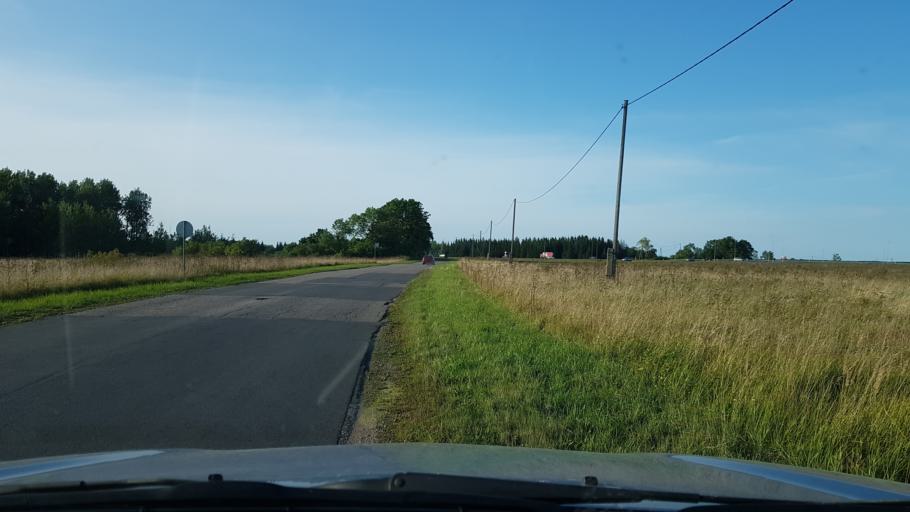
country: EE
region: Ida-Virumaa
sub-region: Narva-Joesuu linn
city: Narva-Joesuu
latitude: 59.3880
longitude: 28.0917
